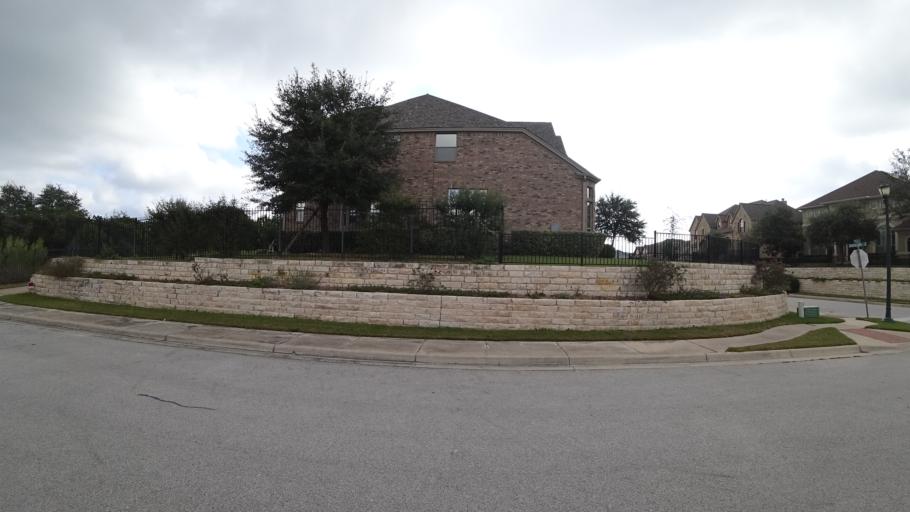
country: US
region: Texas
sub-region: Travis County
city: Barton Creek
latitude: 30.3156
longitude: -97.8963
